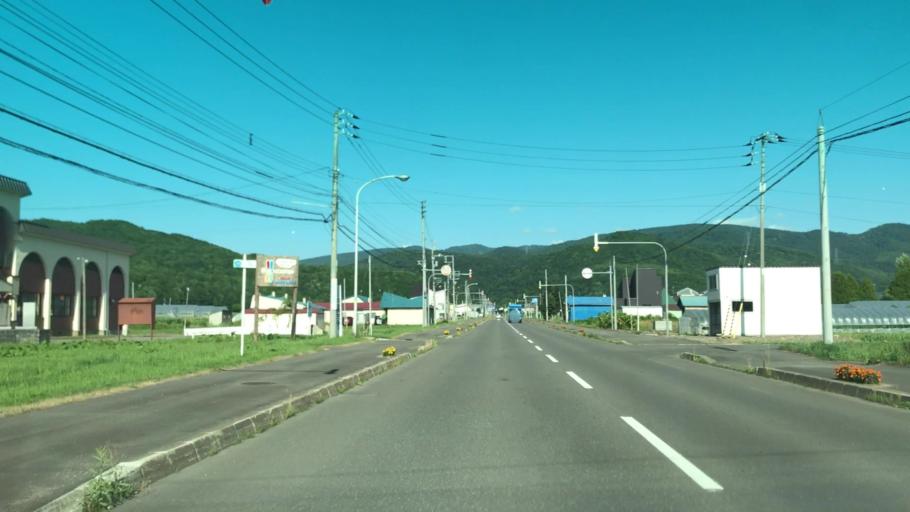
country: JP
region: Hokkaido
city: Yoichi
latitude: 43.0508
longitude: 140.8321
